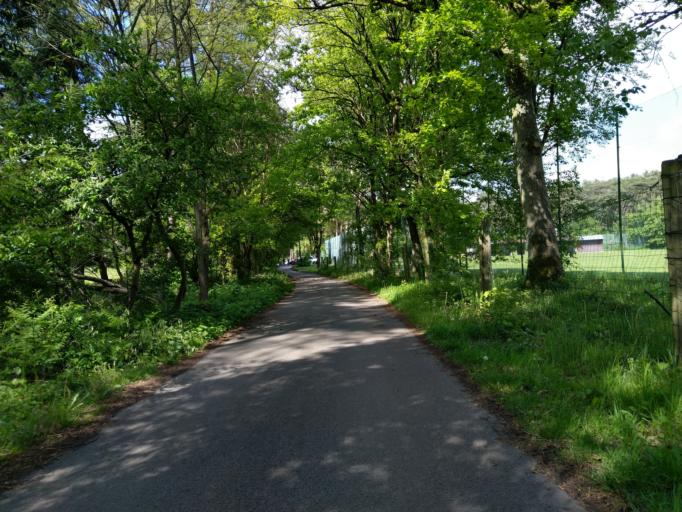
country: BE
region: Wallonia
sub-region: Province du Hainaut
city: Jurbise
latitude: 50.5029
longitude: 3.9269
